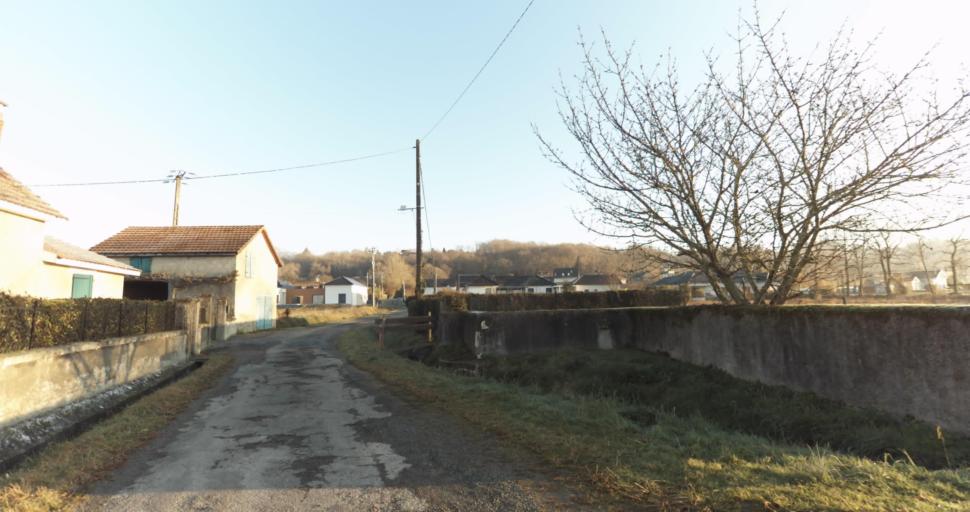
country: FR
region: Aquitaine
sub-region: Departement des Pyrenees-Atlantiques
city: Morlaas
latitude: 43.3277
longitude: -0.2802
